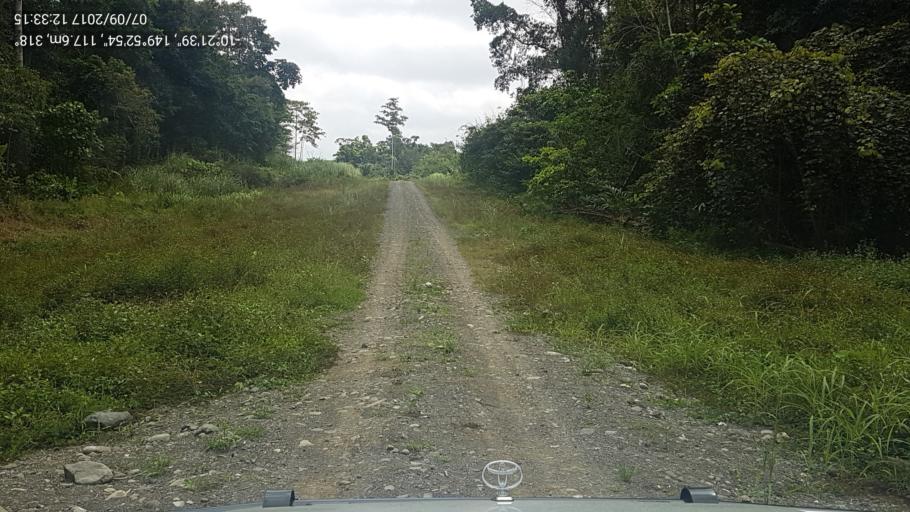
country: PG
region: Milne Bay
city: Alotau
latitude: -10.3610
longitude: 149.8819
